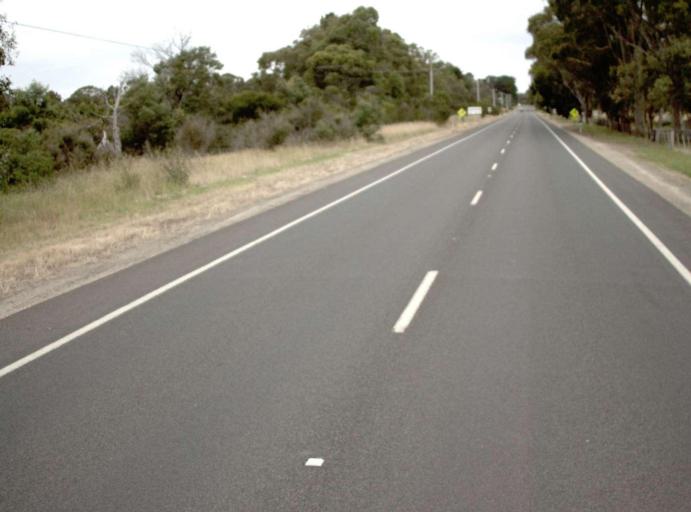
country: AU
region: Victoria
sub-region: Wellington
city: Sale
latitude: -38.1657
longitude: 147.0868
